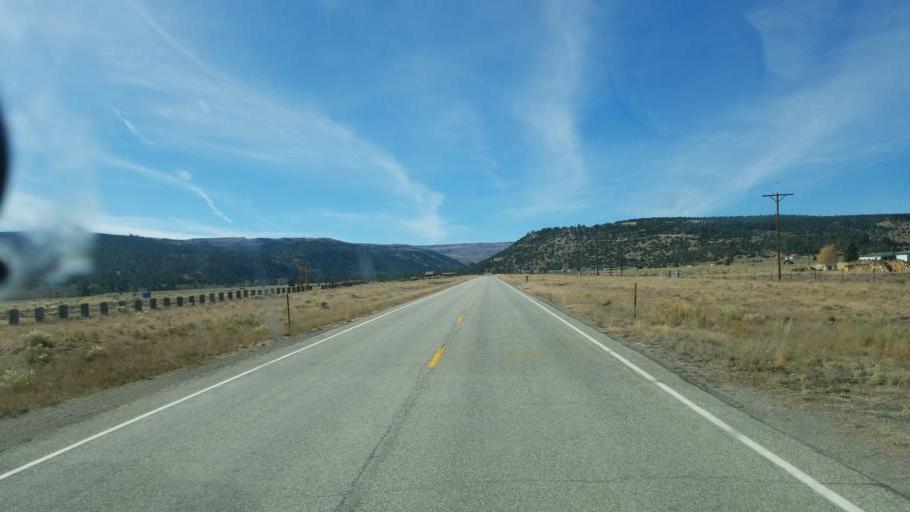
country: US
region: Colorado
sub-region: Conejos County
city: Conejos
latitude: 37.0672
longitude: -106.2084
